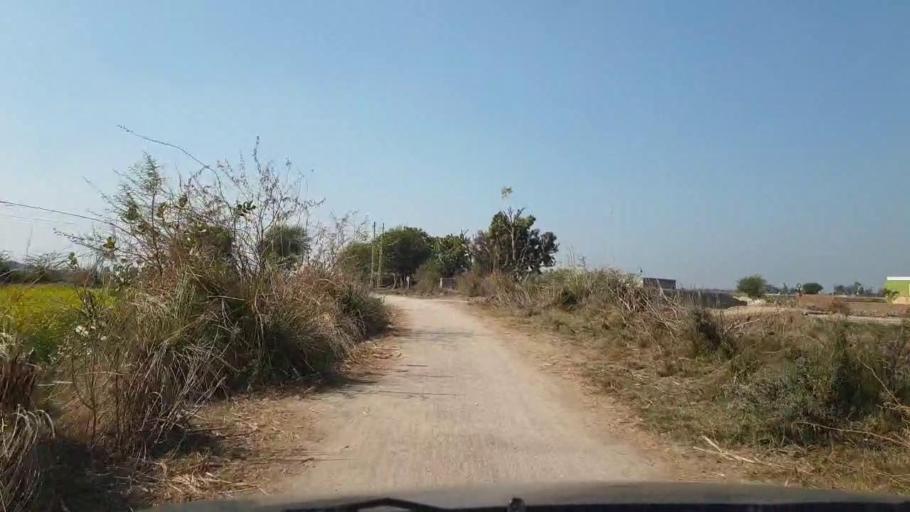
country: PK
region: Sindh
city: Jhol
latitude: 25.9126
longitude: 68.8161
